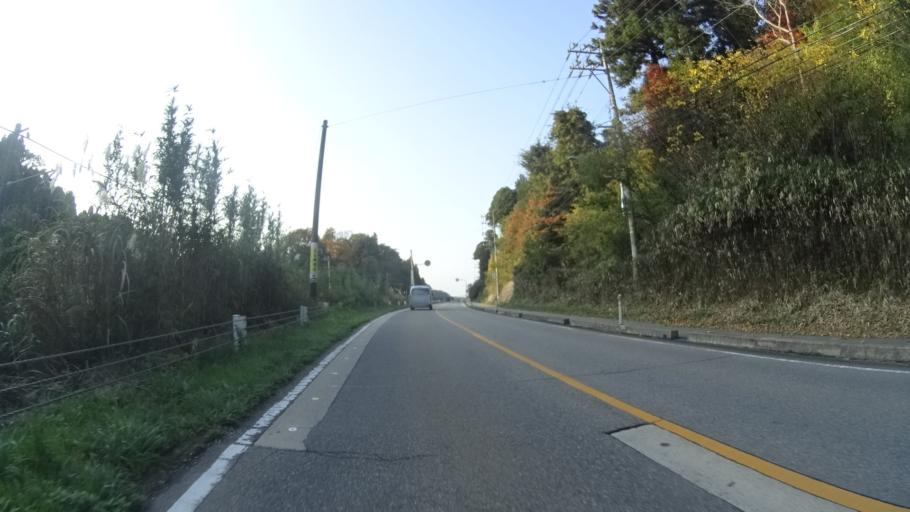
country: JP
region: Ishikawa
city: Nanao
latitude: 37.0579
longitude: 136.9475
